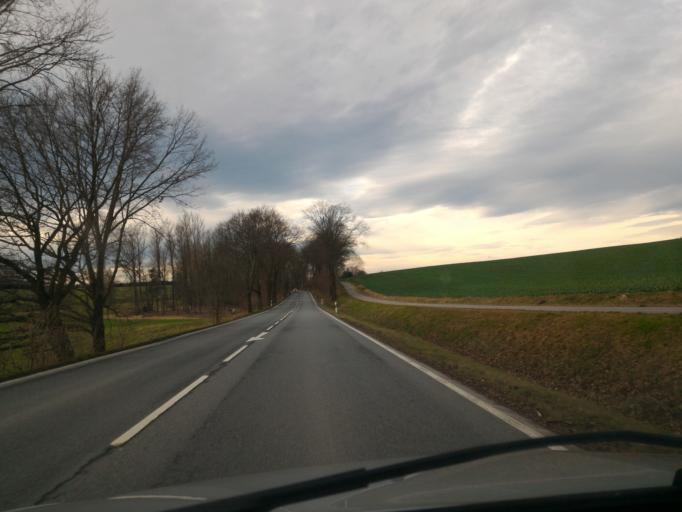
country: DE
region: Saxony
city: Bischofswerda
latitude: 51.1181
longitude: 14.1572
